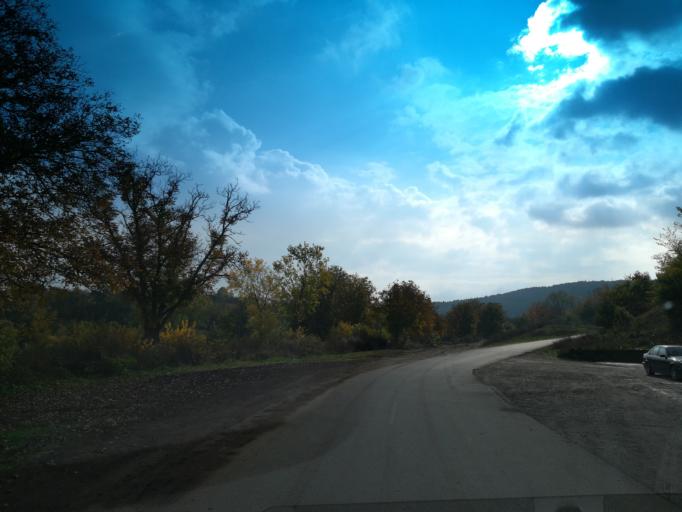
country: BG
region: Stara Zagora
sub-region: Obshtina Nikolaevo
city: Elkhovo
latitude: 42.3388
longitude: 25.4061
